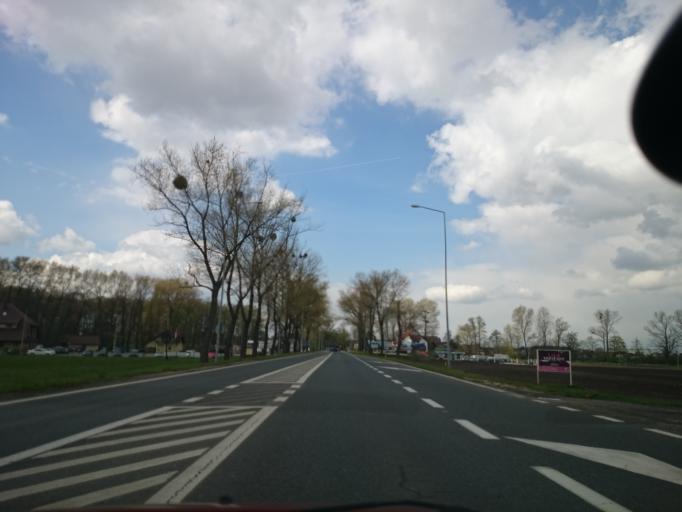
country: PL
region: Opole Voivodeship
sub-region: Powiat opolski
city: Opole
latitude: 50.6418
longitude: 17.9940
